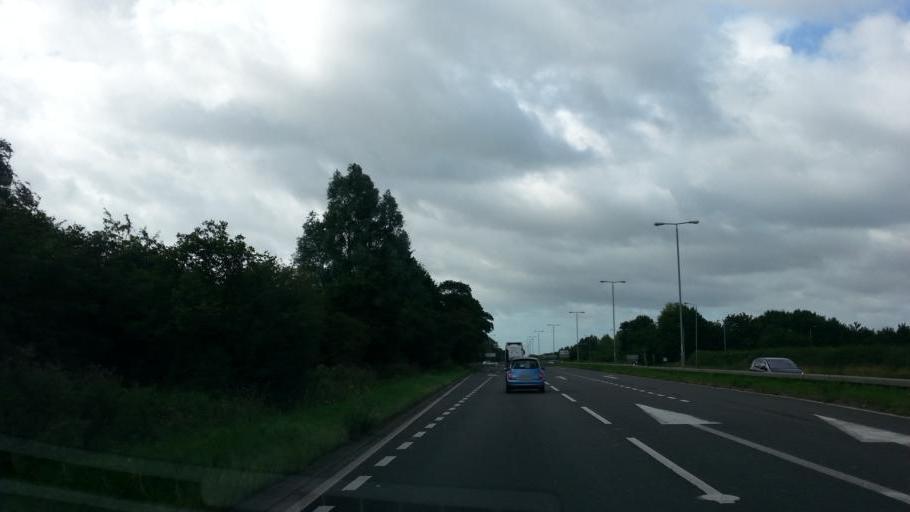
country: GB
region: England
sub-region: Leicestershire
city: Queniborough
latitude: 52.7446
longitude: -1.0640
